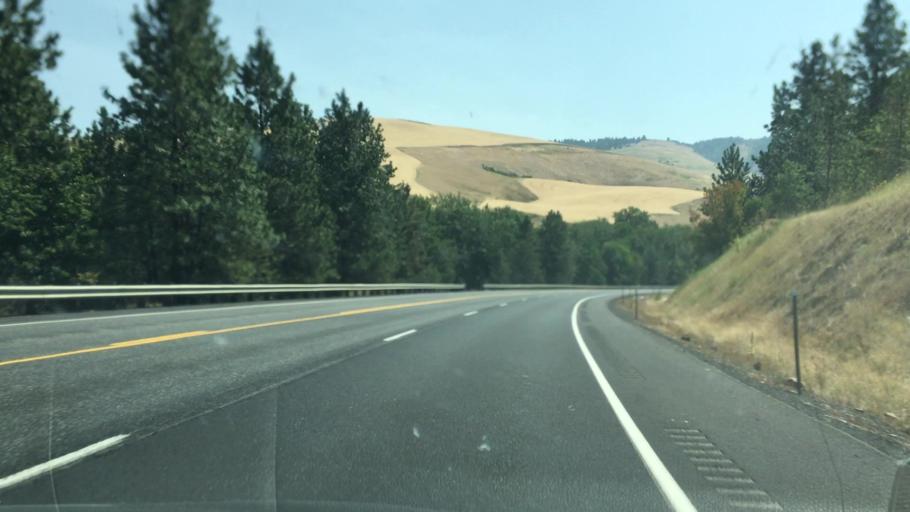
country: US
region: Idaho
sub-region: Nez Perce County
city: Lapwai
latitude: 46.3724
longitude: -116.6558
